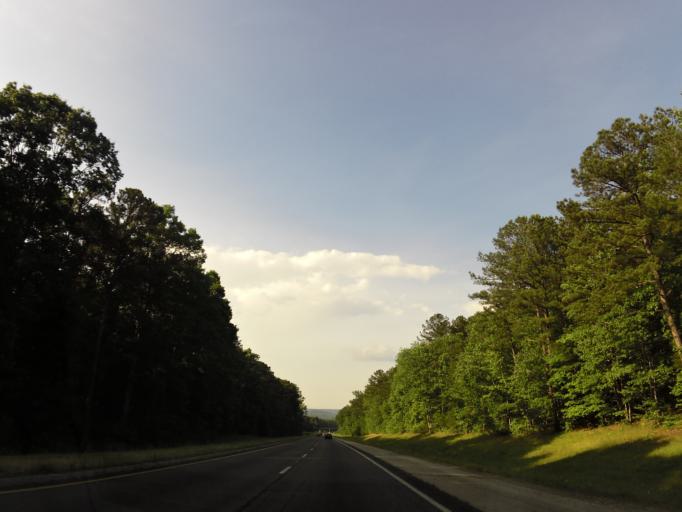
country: US
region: Alabama
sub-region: Saint Clair County
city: Springville
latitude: 33.7374
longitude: -86.4901
